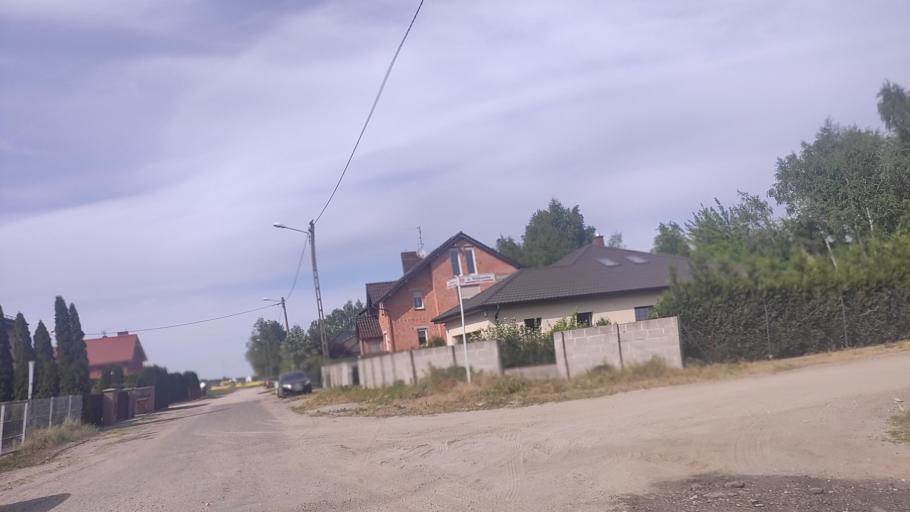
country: PL
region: Greater Poland Voivodeship
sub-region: Powiat poznanski
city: Swarzedz
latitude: 52.4114
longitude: 17.0965
